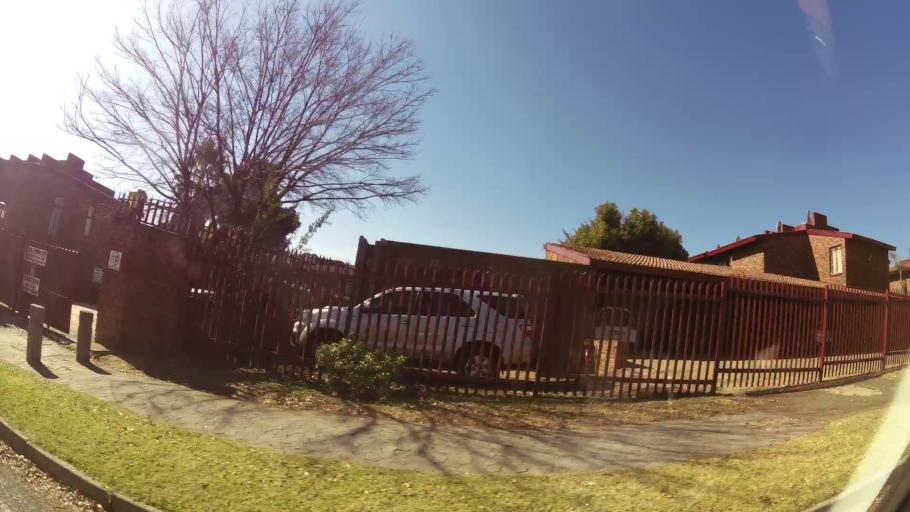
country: ZA
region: Gauteng
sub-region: City of Johannesburg Metropolitan Municipality
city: Johannesburg
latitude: -26.2561
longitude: 28.0678
